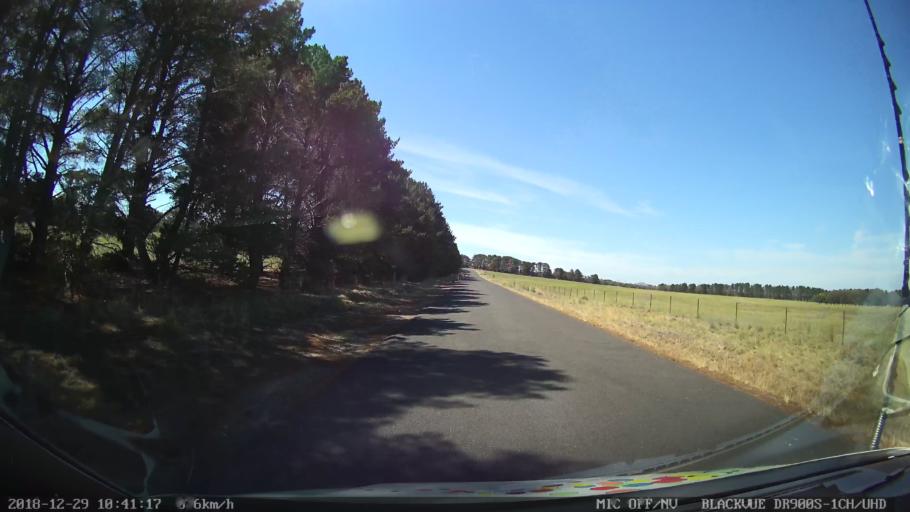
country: AU
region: New South Wales
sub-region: Palerang
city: Bungendore
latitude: -35.0237
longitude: 149.5208
